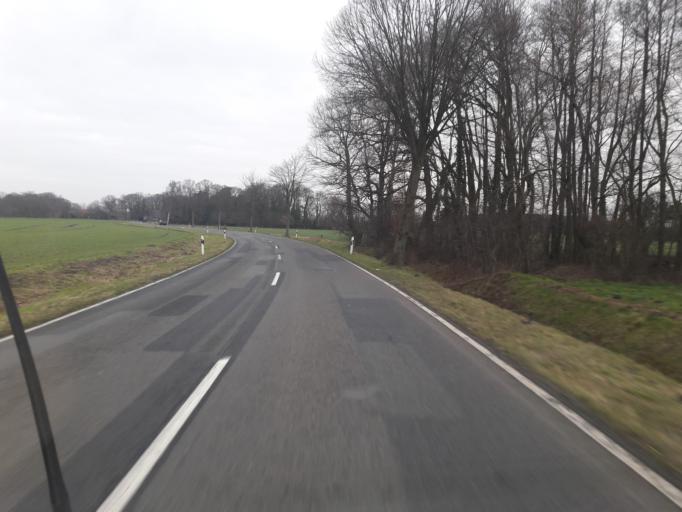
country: DE
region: Lower Saxony
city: Warmsen
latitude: 52.4050
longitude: 8.8603
